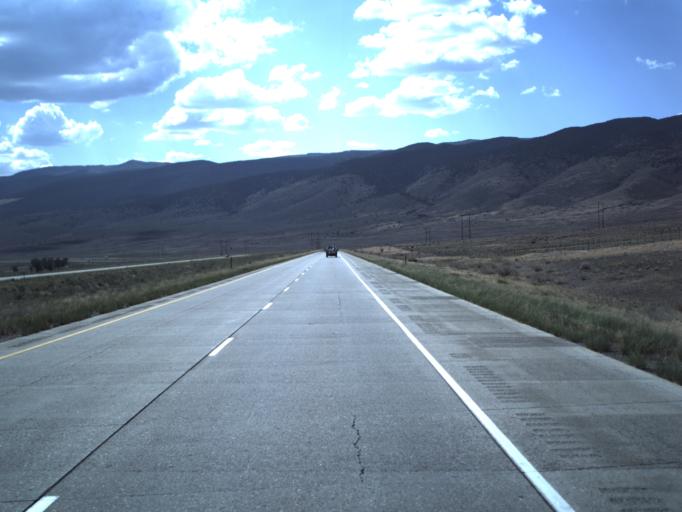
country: US
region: Utah
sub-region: Sevier County
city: Monroe
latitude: 38.6590
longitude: -112.1883
